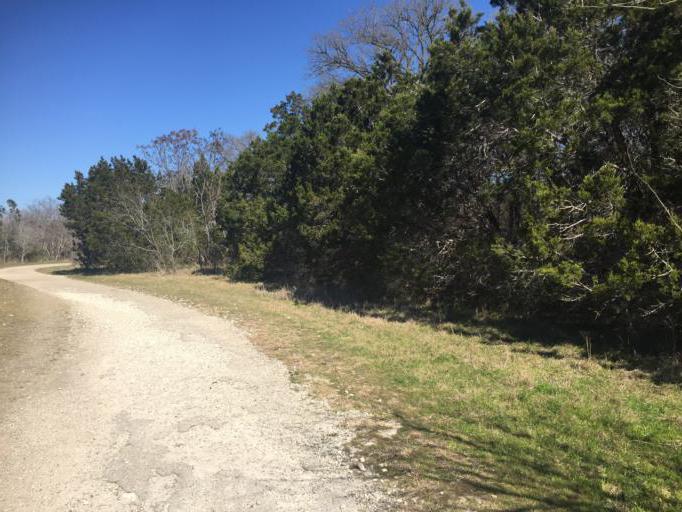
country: US
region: Texas
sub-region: Travis County
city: Onion Creek
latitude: 30.1559
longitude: -97.8063
